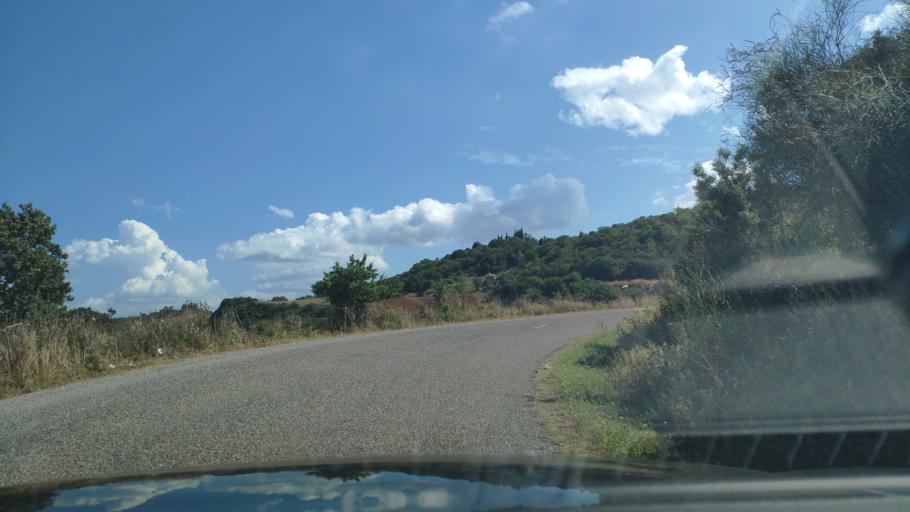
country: GR
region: West Greece
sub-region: Nomos Aitolias kai Akarnanias
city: Katouna
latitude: 38.8051
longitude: 21.1119
